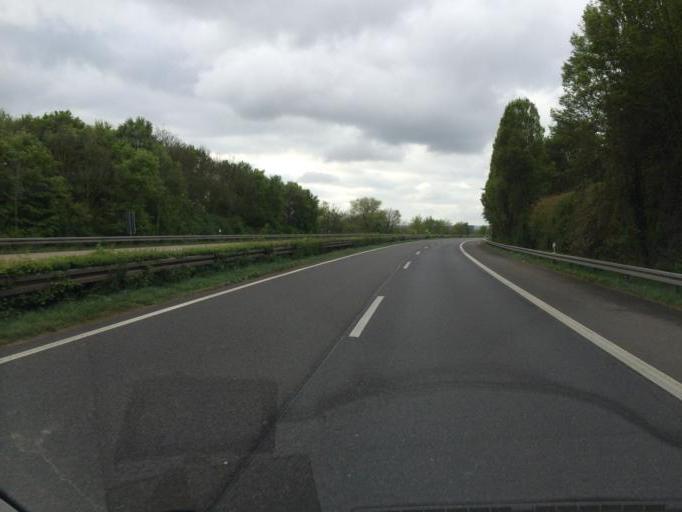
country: DE
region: North Rhine-Westphalia
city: Bruhl
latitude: 50.8244
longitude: 6.9335
